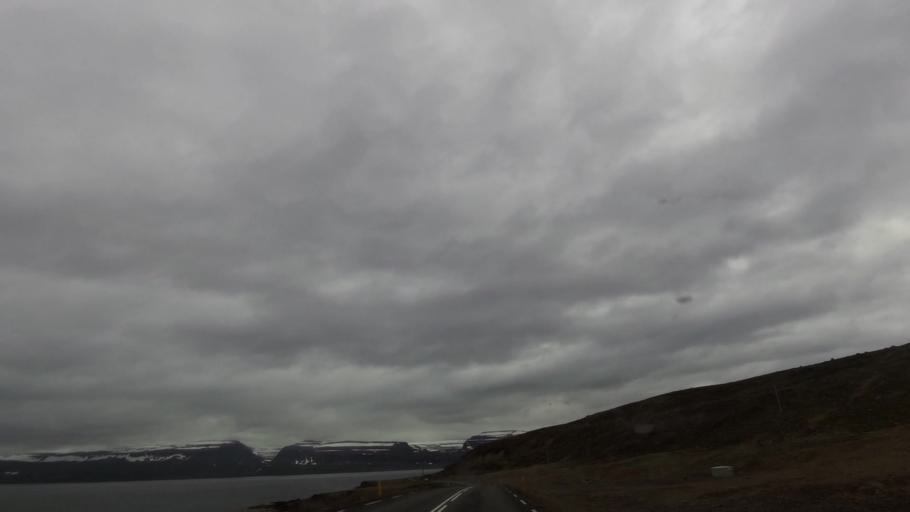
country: IS
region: Westfjords
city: Isafjoerdur
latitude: 66.0480
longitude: -22.7691
